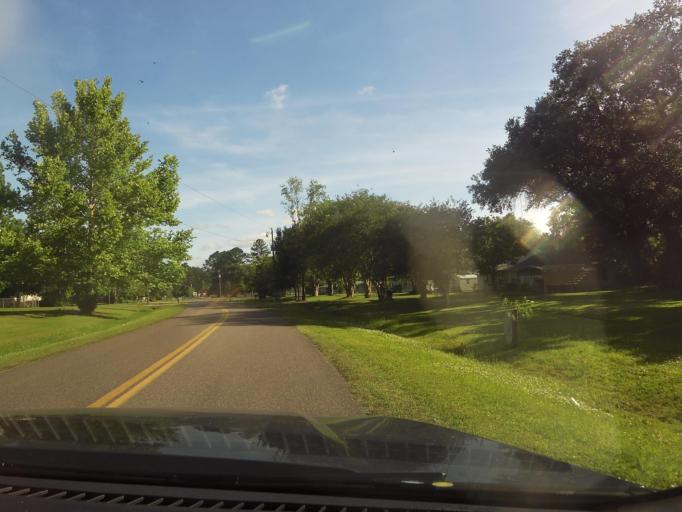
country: US
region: Florida
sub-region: Nassau County
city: Nassau Village-Ratliff
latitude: 30.5202
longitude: -81.7796
